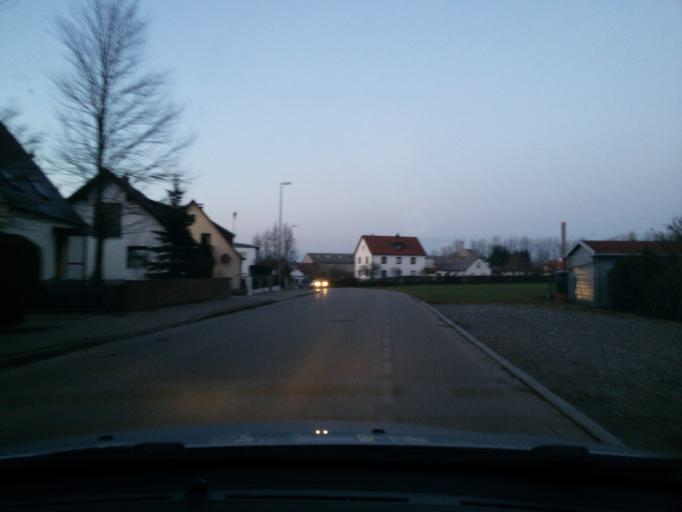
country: DE
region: Bavaria
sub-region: Swabia
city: Schwabmunchen
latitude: 48.1894
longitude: 10.7563
